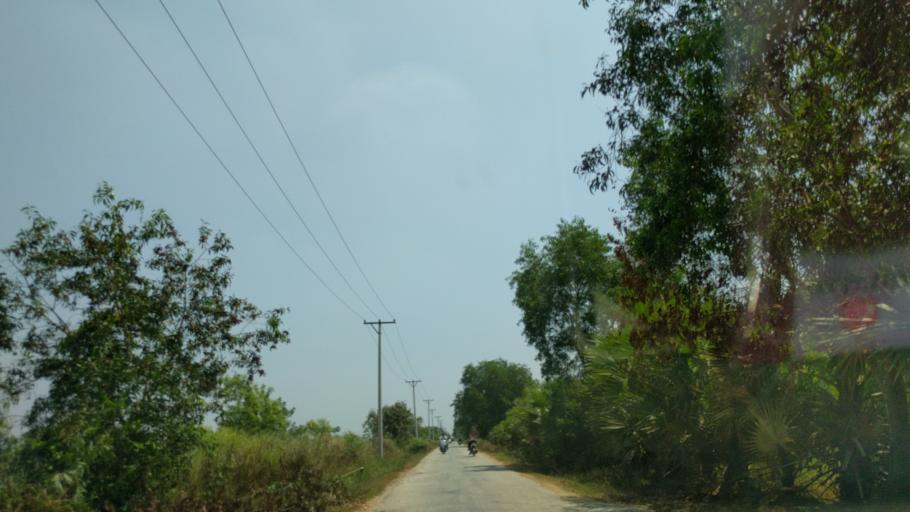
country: MM
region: Mon
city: Martaban
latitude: 16.5856
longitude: 97.6637
